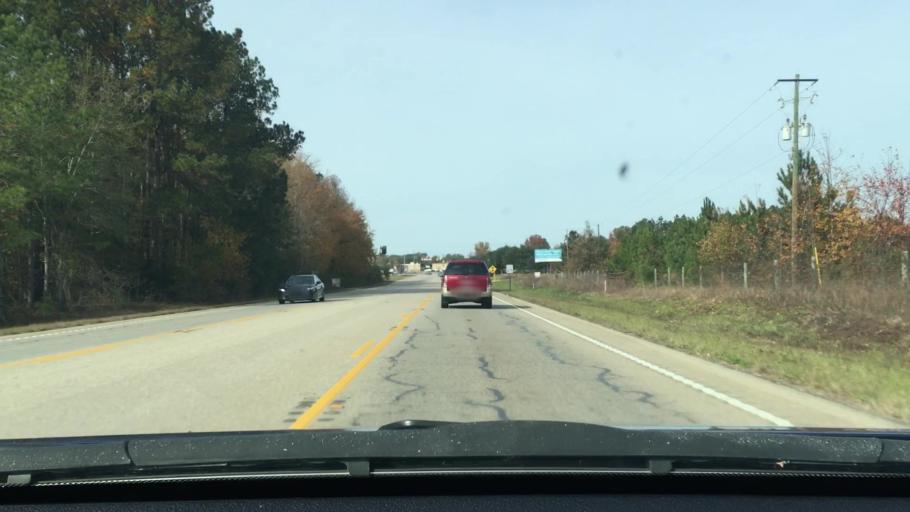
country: US
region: South Carolina
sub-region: Sumter County
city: Oakland
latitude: 33.9481
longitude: -80.4957
